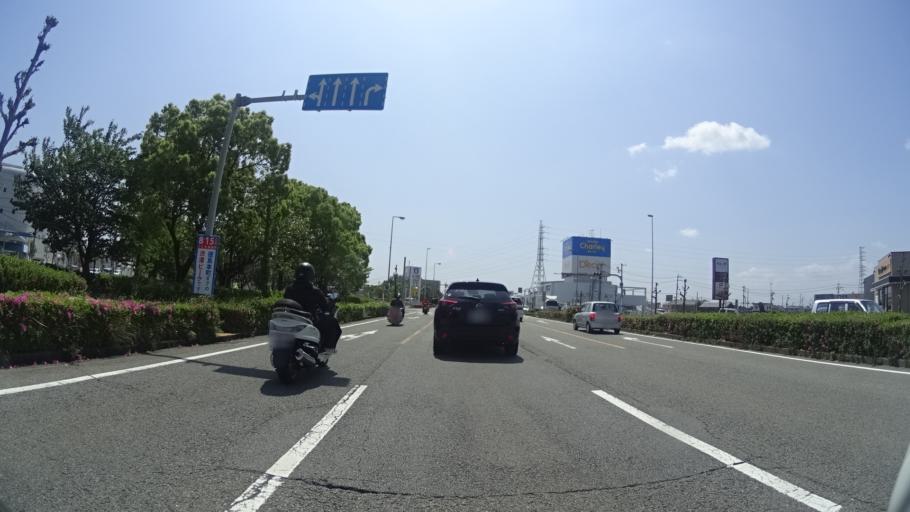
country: JP
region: Tokushima
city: Tokushima-shi
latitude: 34.1243
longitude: 134.5758
